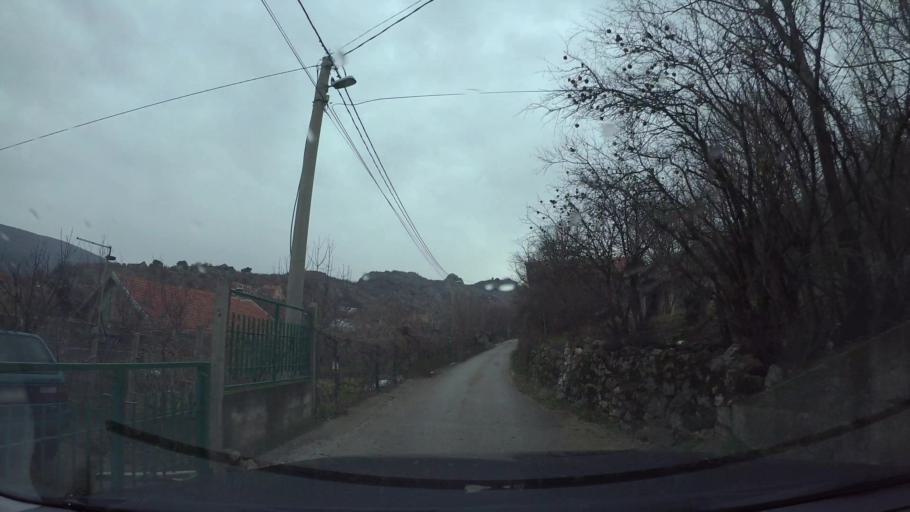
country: BA
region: Federation of Bosnia and Herzegovina
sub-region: Hercegovacko-Bosanski Kanton
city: Mostar
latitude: 43.3593
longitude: 17.8177
